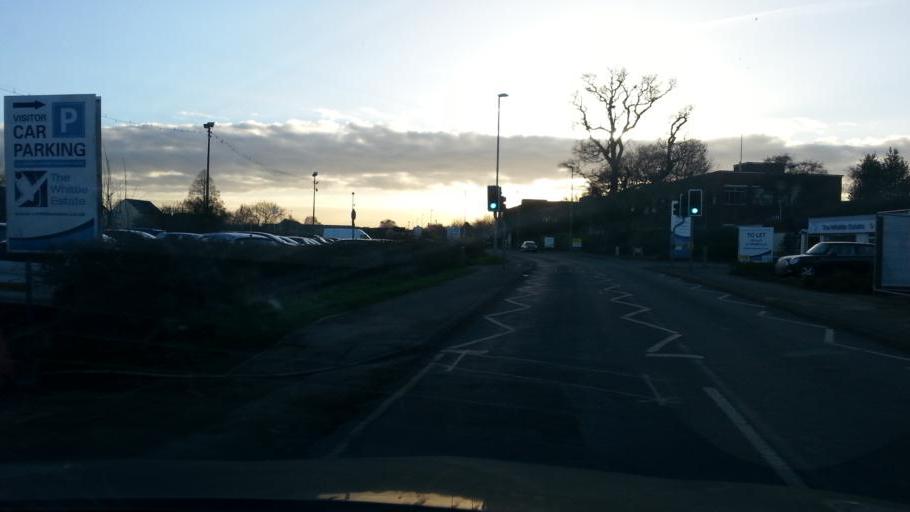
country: GB
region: England
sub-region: Leicestershire
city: Blaby
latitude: 52.5661
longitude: -1.1791
